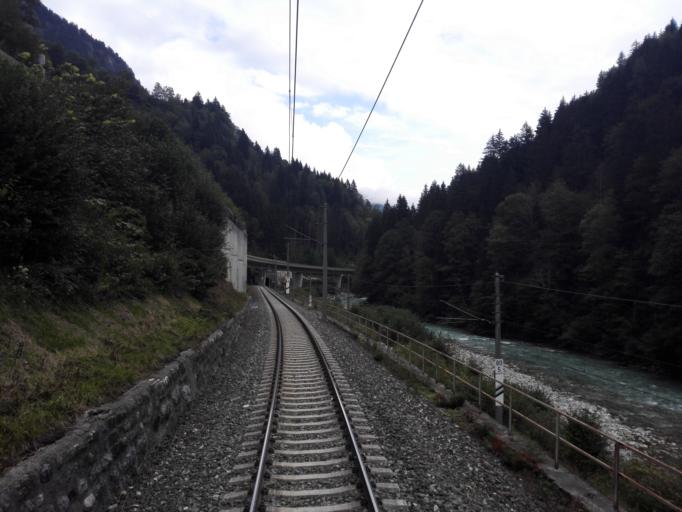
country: AT
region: Salzburg
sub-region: Politischer Bezirk Zell am See
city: Taxenbach
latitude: 47.2993
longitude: 12.9930
